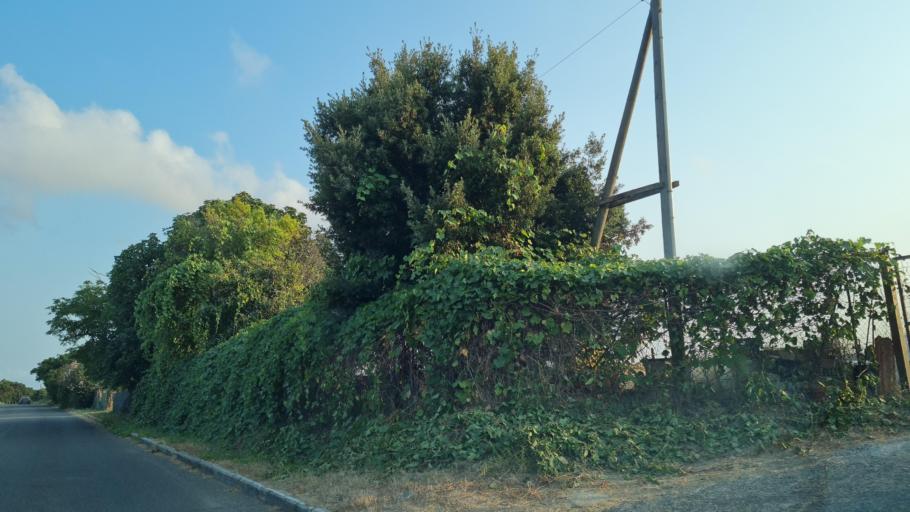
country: IT
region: Latium
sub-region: Provincia di Viterbo
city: Montalto di Castro
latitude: 42.3446
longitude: 11.6098
